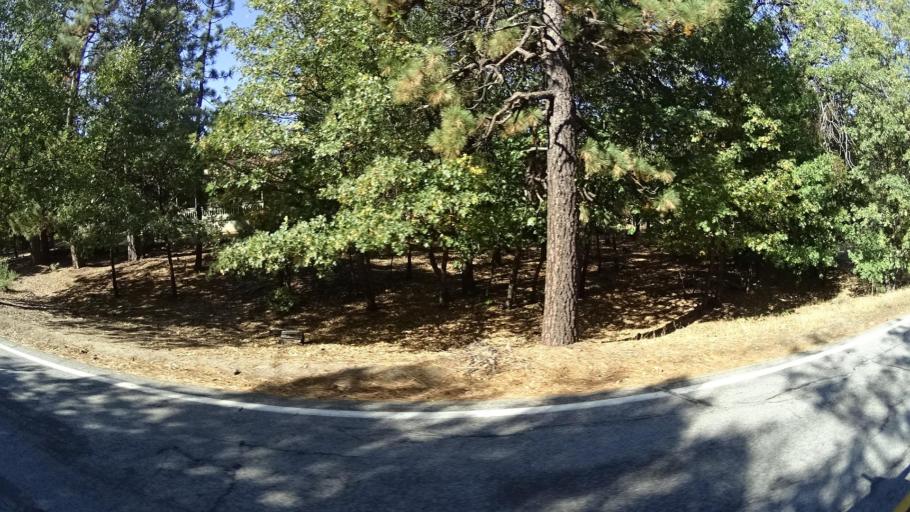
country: US
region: California
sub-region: San Diego County
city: Pine Valley
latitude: 32.8722
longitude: -116.4165
